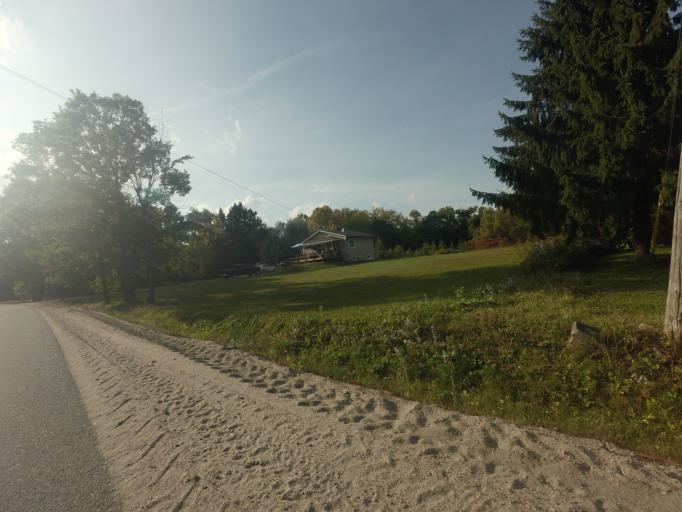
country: CA
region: Quebec
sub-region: Outaouais
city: Maniwaki
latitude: 46.3658
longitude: -75.9974
